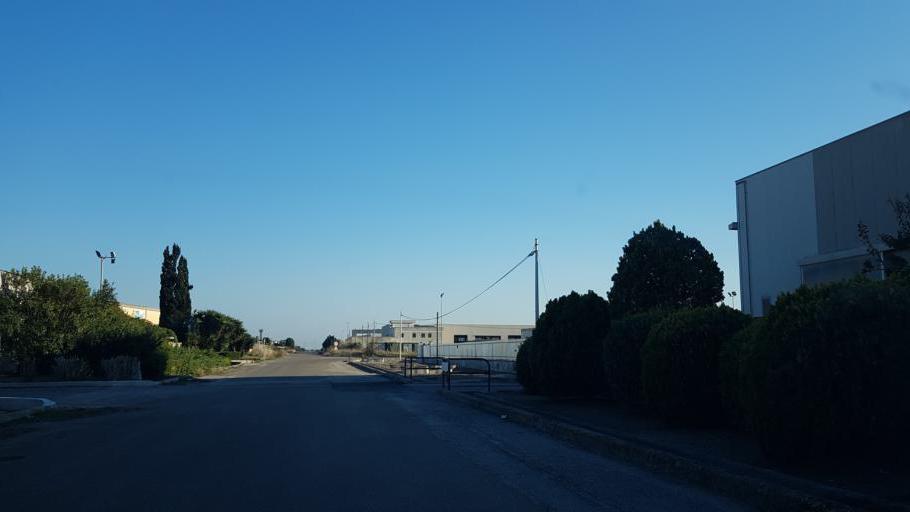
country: IT
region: Apulia
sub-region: Provincia di Brindisi
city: Materdomini
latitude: 40.6306
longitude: 17.9674
